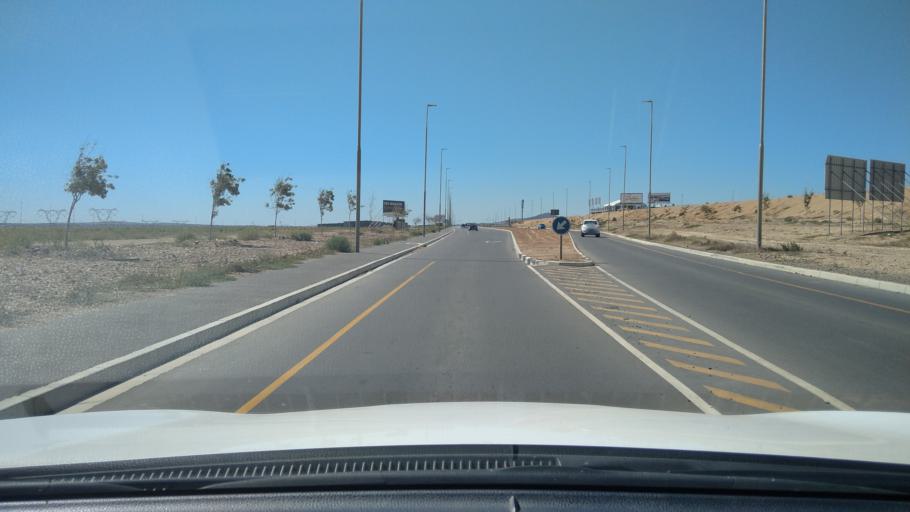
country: ZA
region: Western Cape
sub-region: City of Cape Town
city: Sunset Beach
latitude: -33.8239
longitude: 18.5525
